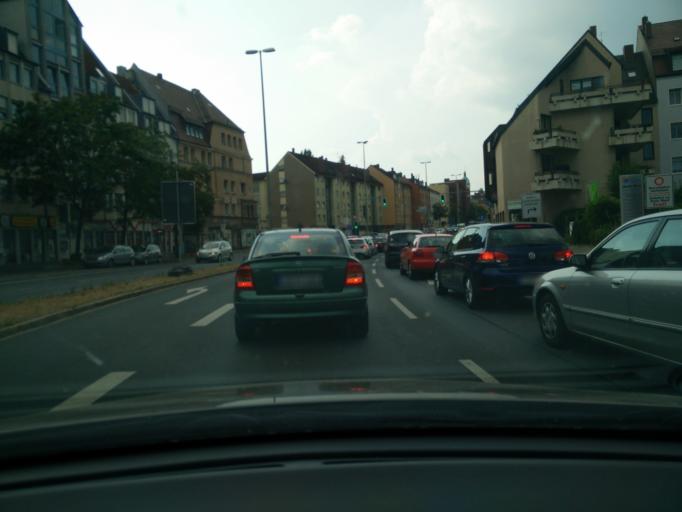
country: DE
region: Bavaria
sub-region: Regierungsbezirk Mittelfranken
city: Nuernberg
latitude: 49.4600
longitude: 11.1068
